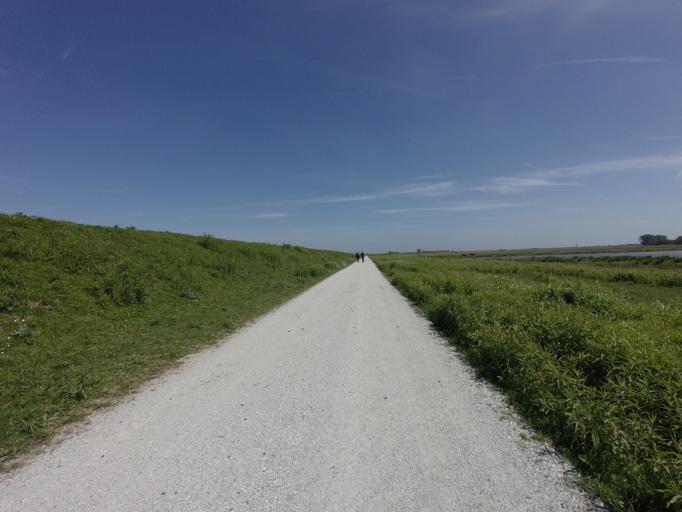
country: NL
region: South Holland
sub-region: Gemeente Spijkenisse
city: Spijkenisse
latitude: 51.7488
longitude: 4.2978
